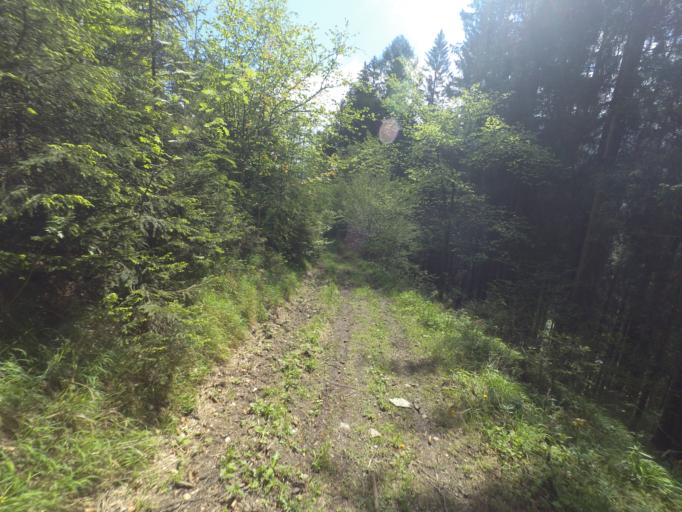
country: AT
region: Salzburg
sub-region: Politischer Bezirk Zell am See
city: Lend
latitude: 47.3047
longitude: 13.0655
